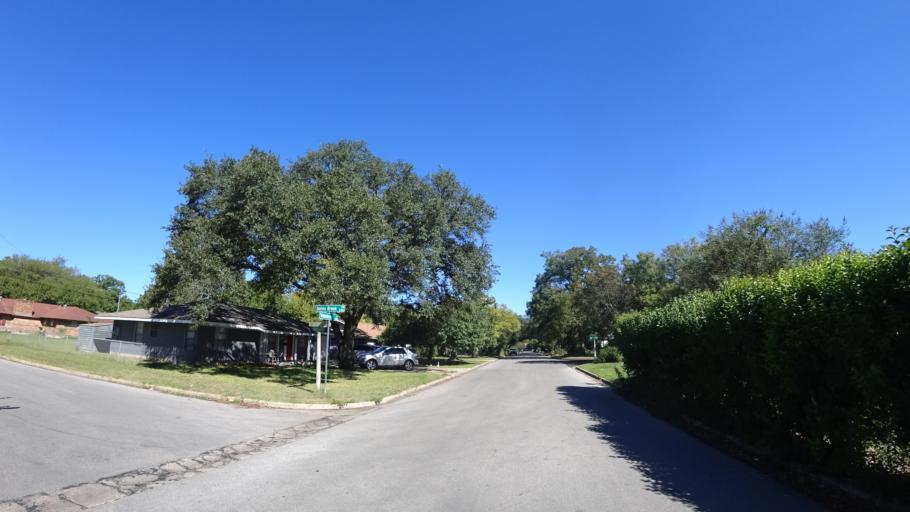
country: US
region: Texas
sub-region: Travis County
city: Austin
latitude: 30.3036
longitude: -97.6895
